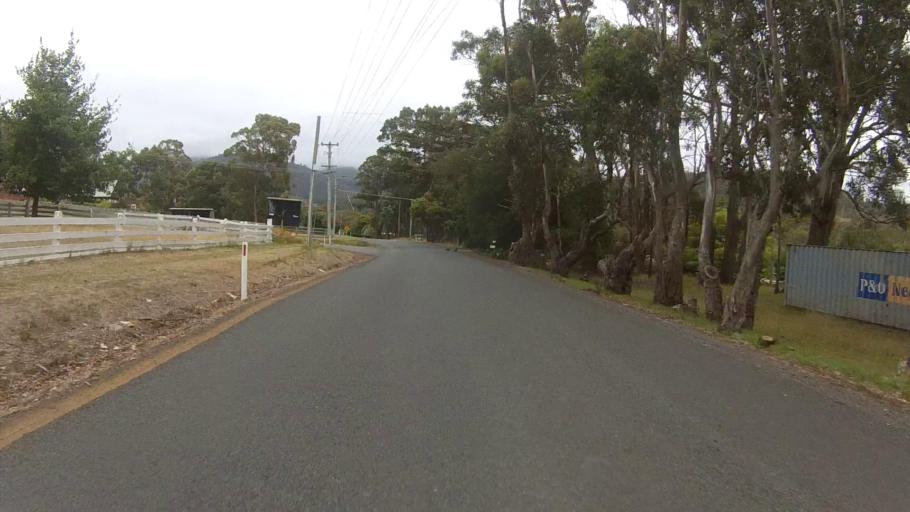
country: AU
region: Tasmania
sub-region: Kingborough
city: Kingston
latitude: -42.9646
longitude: 147.2831
